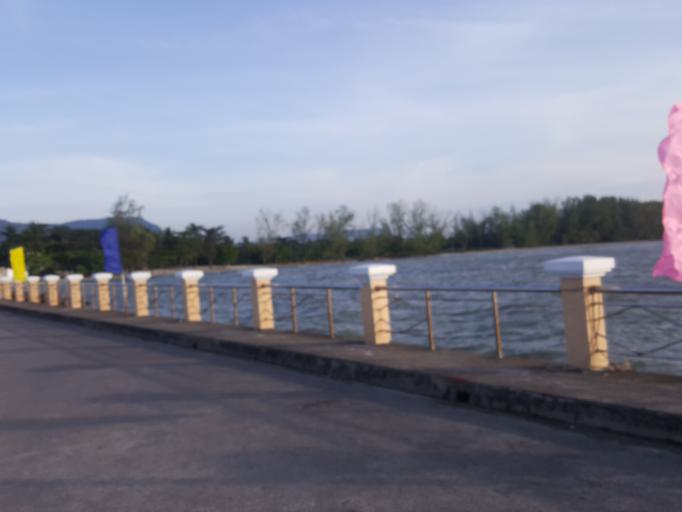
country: VN
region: Kien Giang
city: Duong GJong
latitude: 10.1476
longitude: 104.0381
